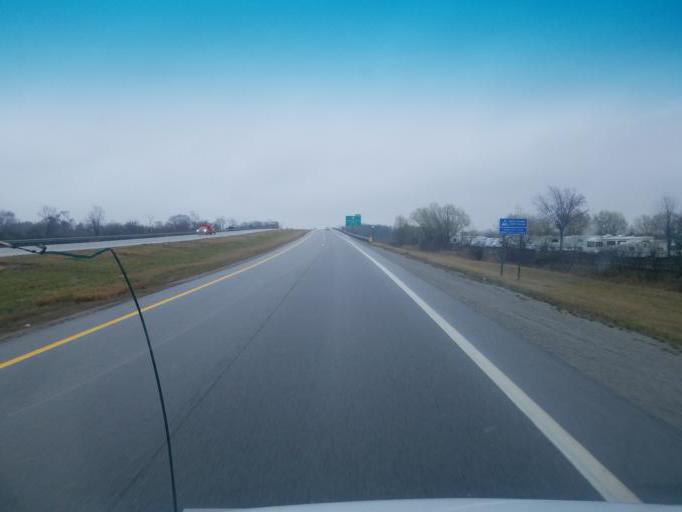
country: US
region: Ohio
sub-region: Wood County
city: Bowling Green
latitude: 41.3491
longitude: -83.6653
